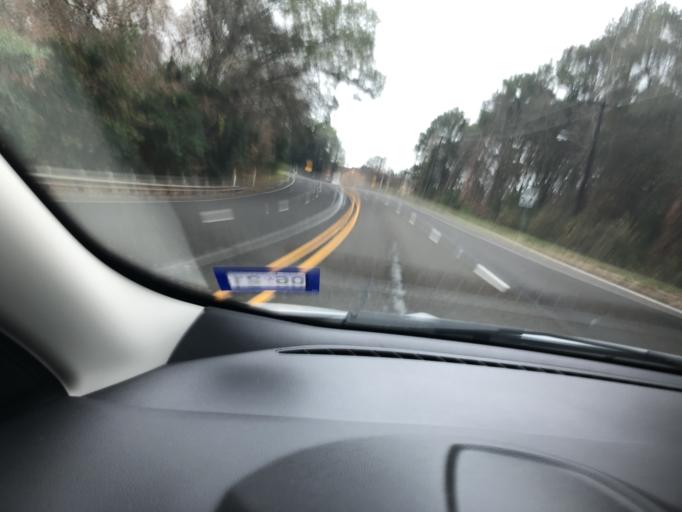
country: US
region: Texas
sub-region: Nacogdoches County
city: Nacogdoches
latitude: 31.6203
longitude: -94.6350
